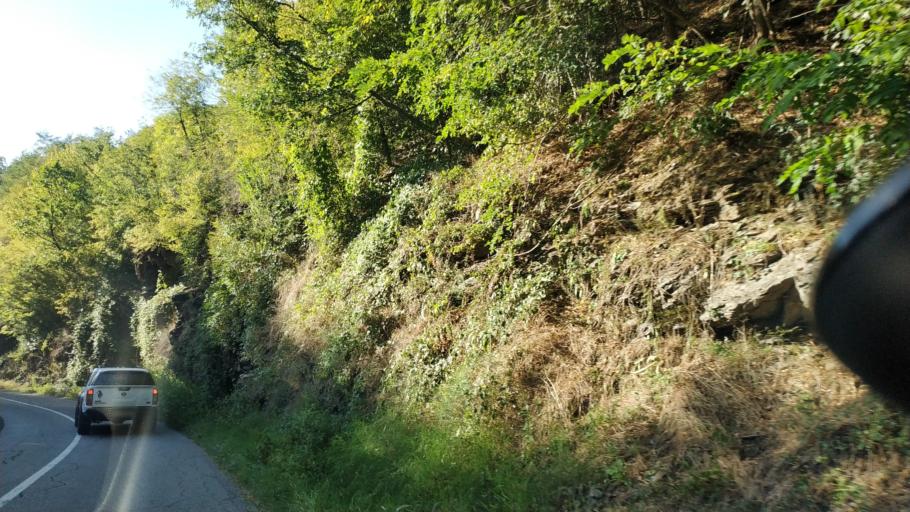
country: RS
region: Central Serbia
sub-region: Rasinski Okrug
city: Krusevac
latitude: 43.4688
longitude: 21.3606
